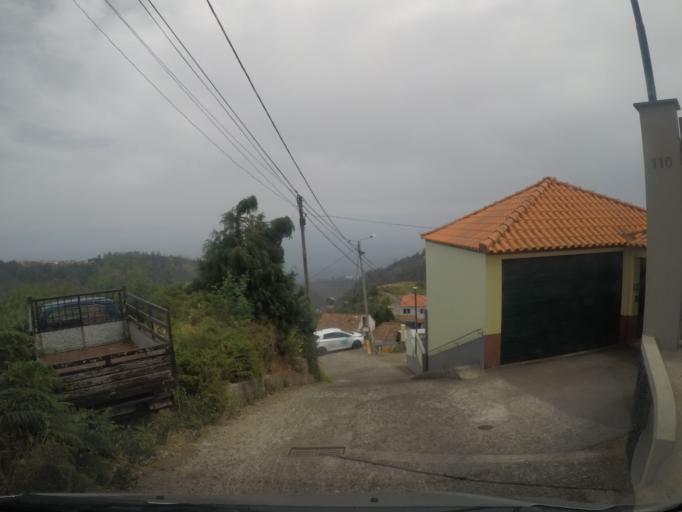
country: PT
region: Madeira
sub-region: Santa Cruz
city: Camacha
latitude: 32.6742
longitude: -16.8388
